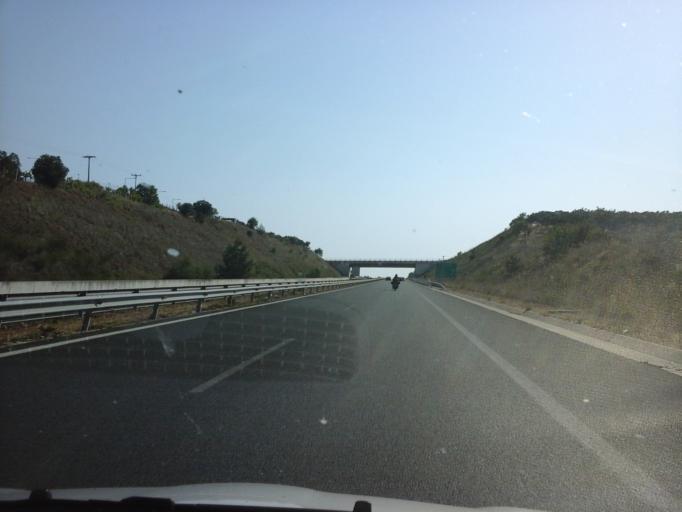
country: GR
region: East Macedonia and Thrace
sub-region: Nomos Evrou
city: Alexandroupoli
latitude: 40.8750
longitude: 25.8475
